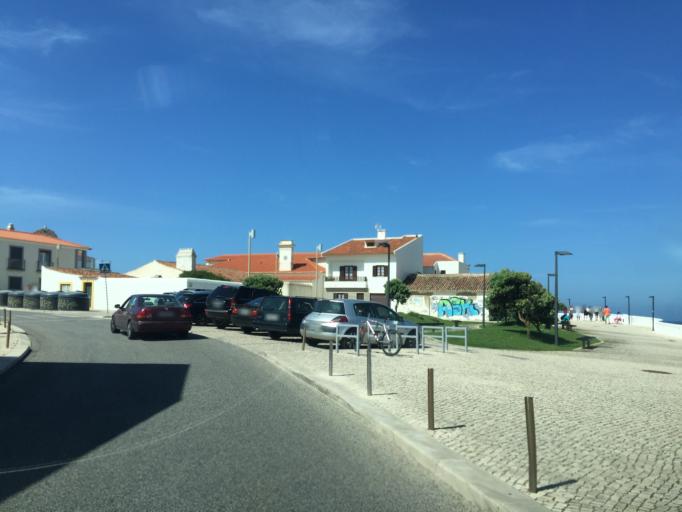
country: PT
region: Lisbon
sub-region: Torres Vedras
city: Silveira
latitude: 39.1361
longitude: -9.3811
